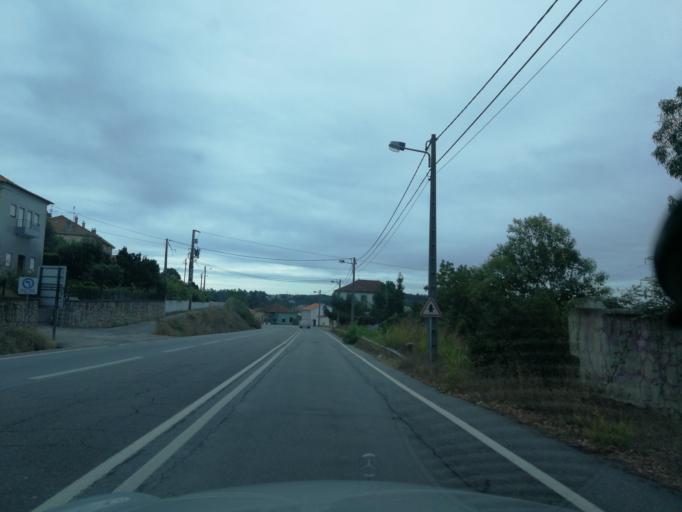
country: PT
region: Aveiro
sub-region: Agueda
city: Agueda
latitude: 40.5804
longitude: -8.4509
